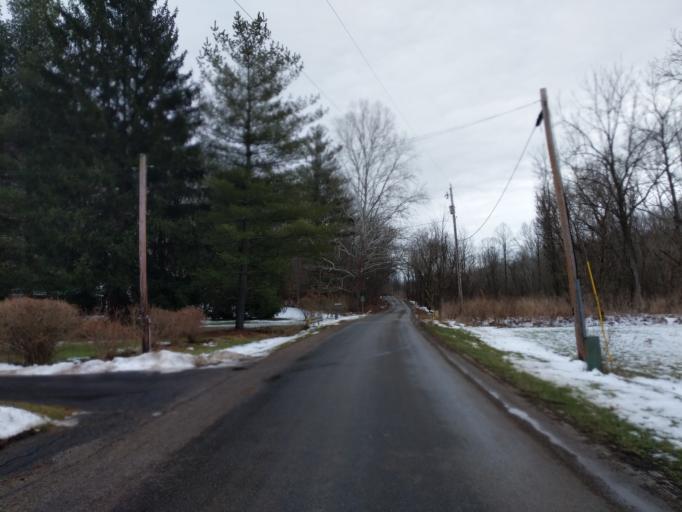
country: US
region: Ohio
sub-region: Athens County
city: The Plains
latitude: 39.3379
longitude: -82.1553
